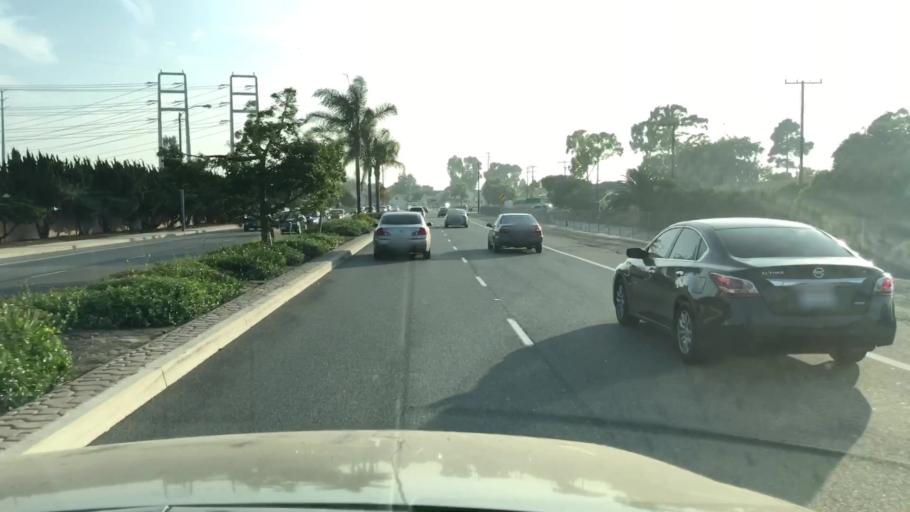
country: US
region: California
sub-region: Ventura County
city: Port Hueneme
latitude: 34.1560
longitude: -119.1637
